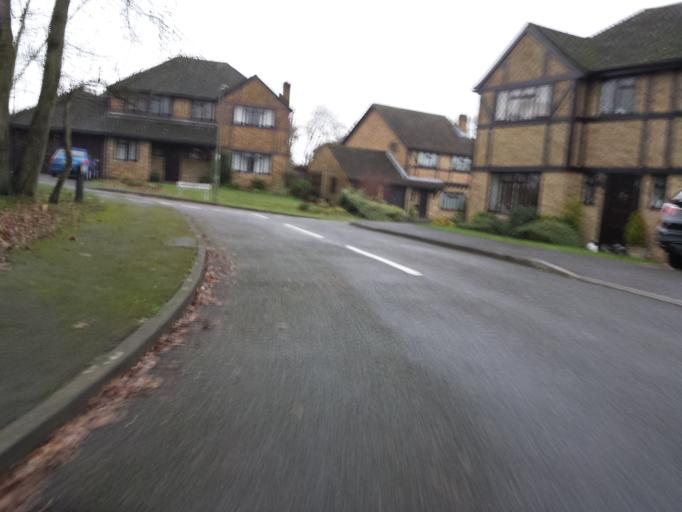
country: GB
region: England
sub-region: Surrey
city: Bagshot
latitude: 51.3528
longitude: -0.6939
